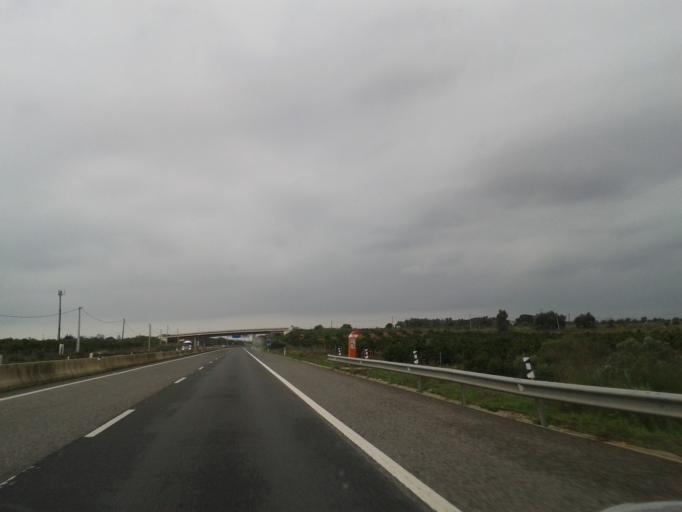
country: PT
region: Faro
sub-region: Lagoa
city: Lagoa
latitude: 37.1517
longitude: -8.4410
